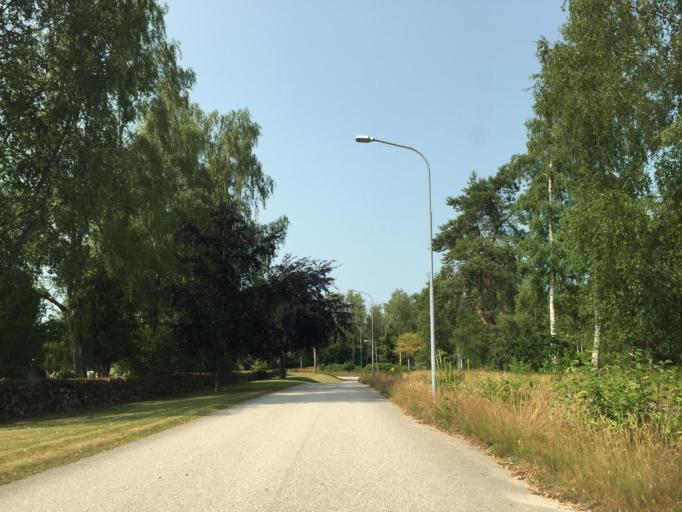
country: SE
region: Vaestra Goetaland
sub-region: Lilla Edets Kommun
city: Lilla Edet
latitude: 58.1788
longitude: 12.1018
